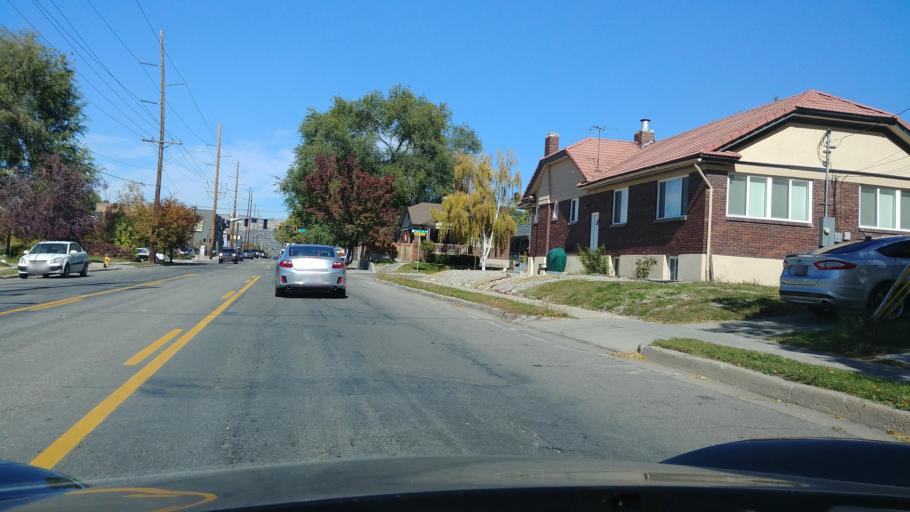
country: US
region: Utah
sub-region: Salt Lake County
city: South Salt Lake
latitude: 40.7213
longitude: -111.8654
